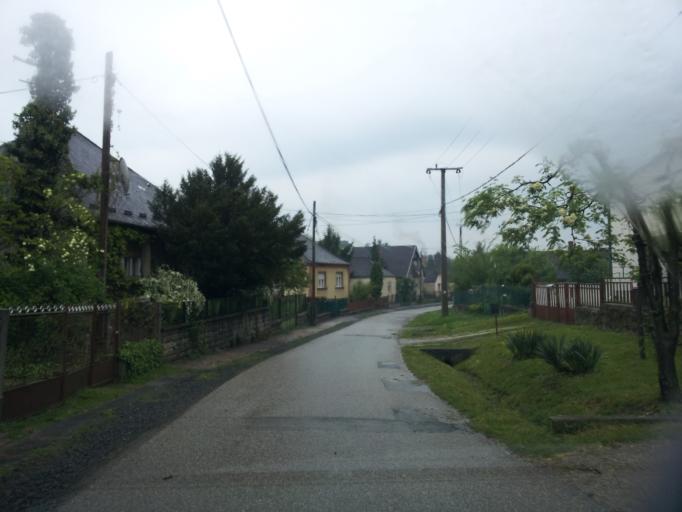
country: HU
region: Baranya
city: Hosszuheteny
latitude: 46.1727
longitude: 18.3486
